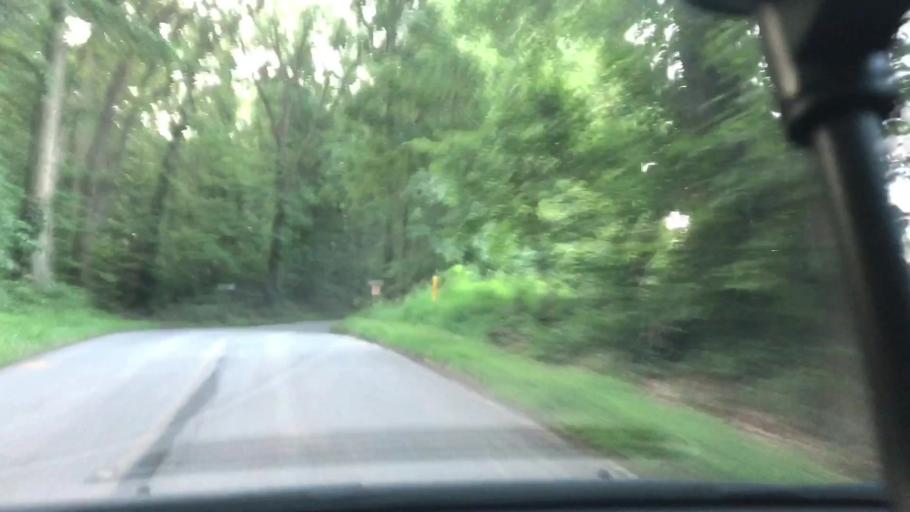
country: US
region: Pennsylvania
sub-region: Chester County
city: Kenilworth
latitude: 40.1886
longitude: -75.6459
